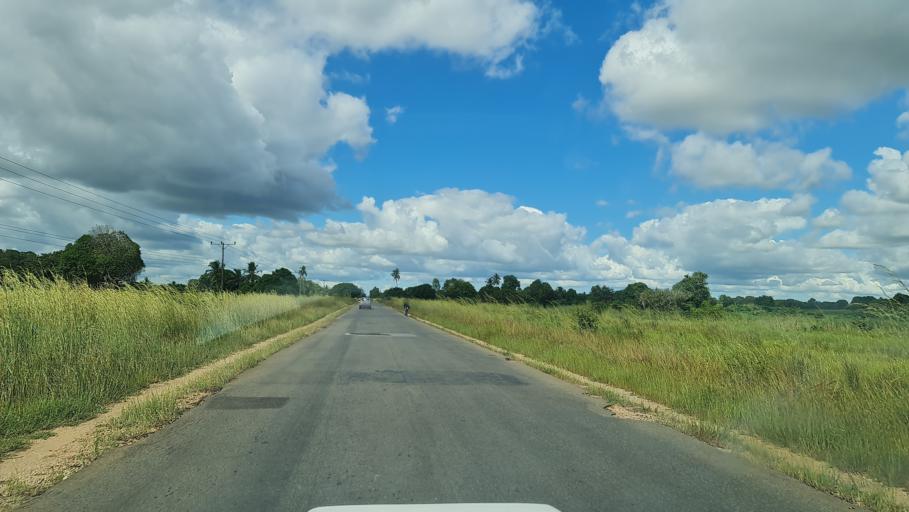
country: MZ
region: Zambezia
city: Quelimane
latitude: -17.5939
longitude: 36.7769
